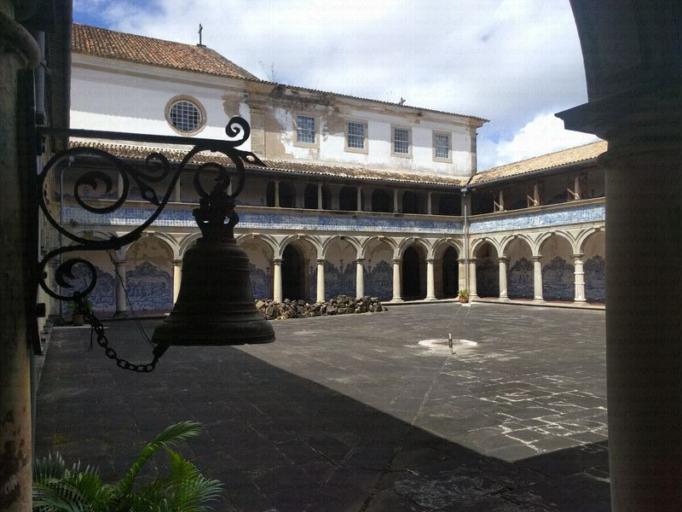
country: BR
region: Bahia
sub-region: Salvador
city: Salvador
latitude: -12.9746
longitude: -38.5094
